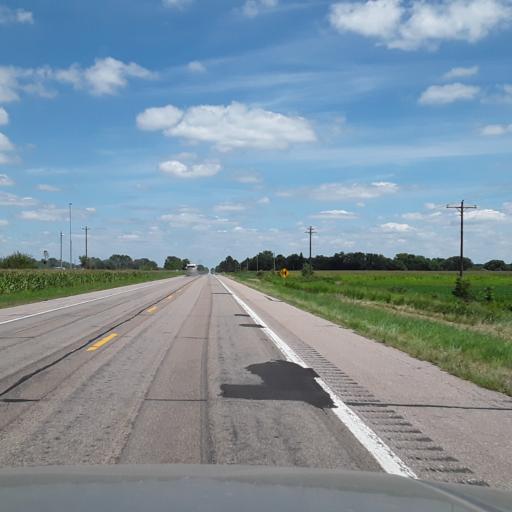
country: US
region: Nebraska
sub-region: Polk County
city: Osceola
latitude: 41.3590
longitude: -97.5621
